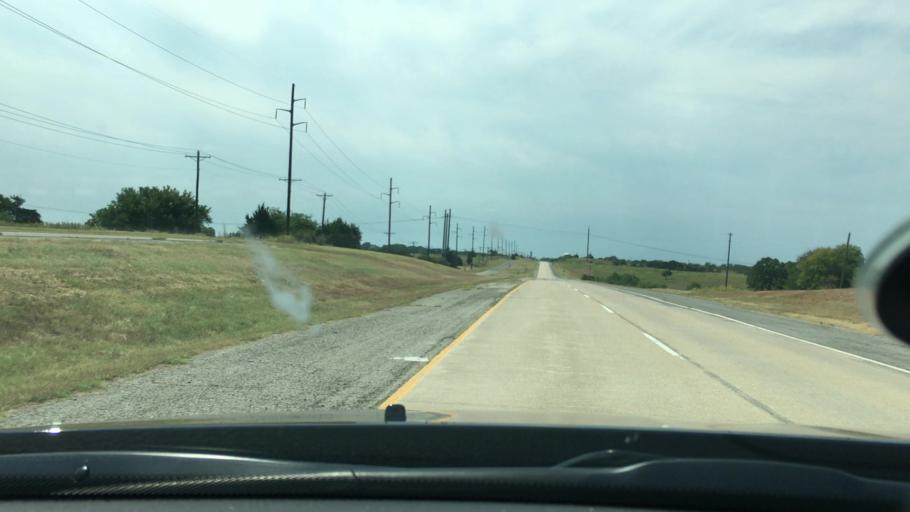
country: US
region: Oklahoma
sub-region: Carter County
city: Ardmore
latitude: 34.2385
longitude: -97.1432
